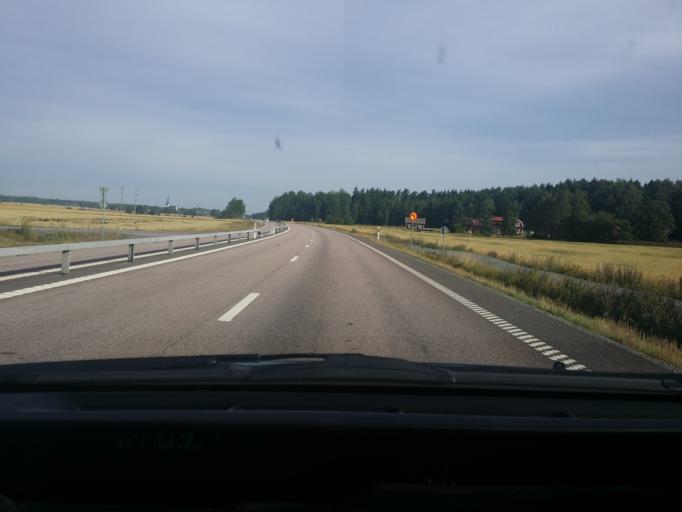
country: SE
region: Vaestmanland
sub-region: Vasteras
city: Tillberga
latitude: 59.7169
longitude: 16.5813
